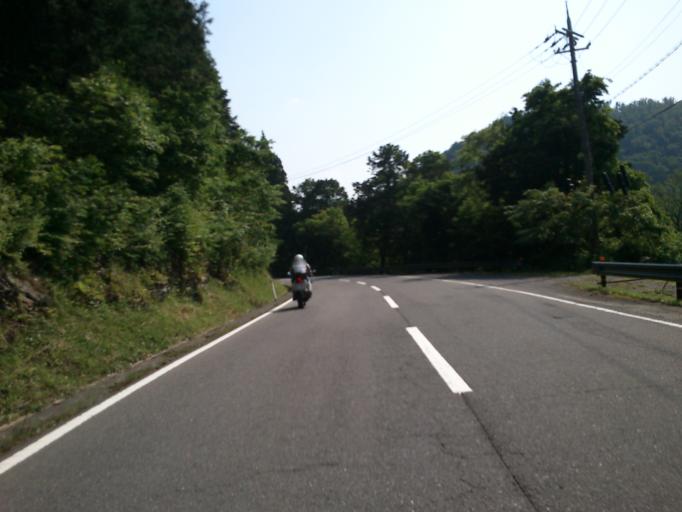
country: JP
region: Kyoto
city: Kameoka
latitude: 35.2631
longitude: 135.5727
